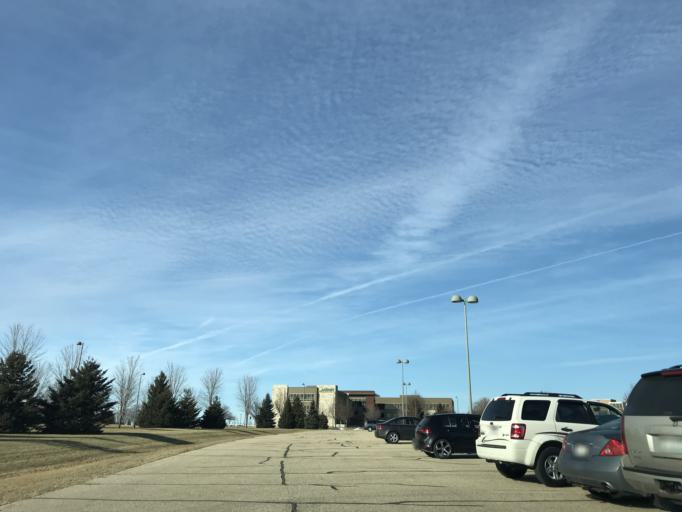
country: US
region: Wisconsin
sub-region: Dane County
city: Windsor
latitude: 43.1470
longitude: -89.2930
